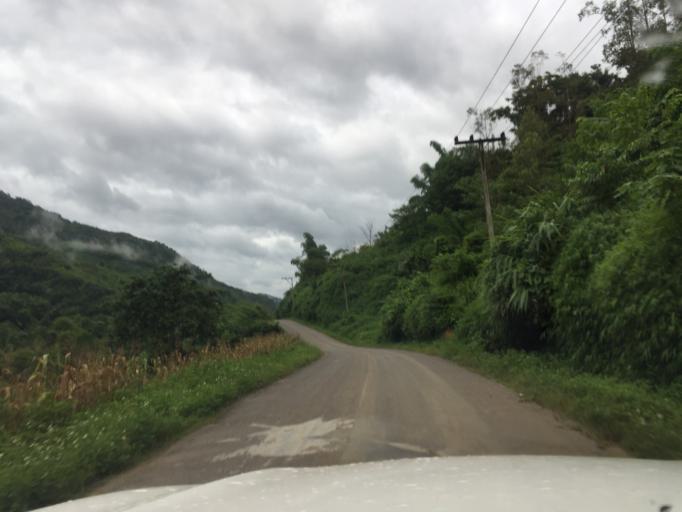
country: LA
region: Oudomxai
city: Muang La
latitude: 20.9999
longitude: 102.2325
